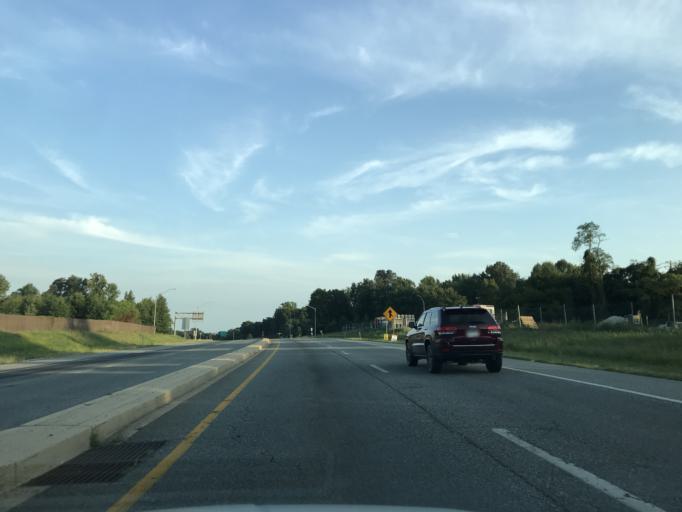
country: US
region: Maryland
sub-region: Cecil County
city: North East
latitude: 39.6347
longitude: -75.9578
